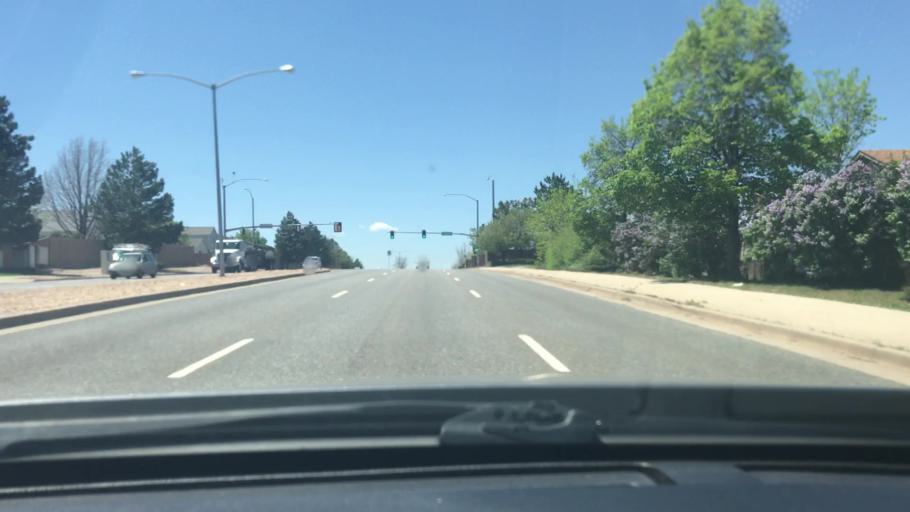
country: US
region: Colorado
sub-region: Arapahoe County
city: Dove Valley
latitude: 39.6531
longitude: -104.7623
